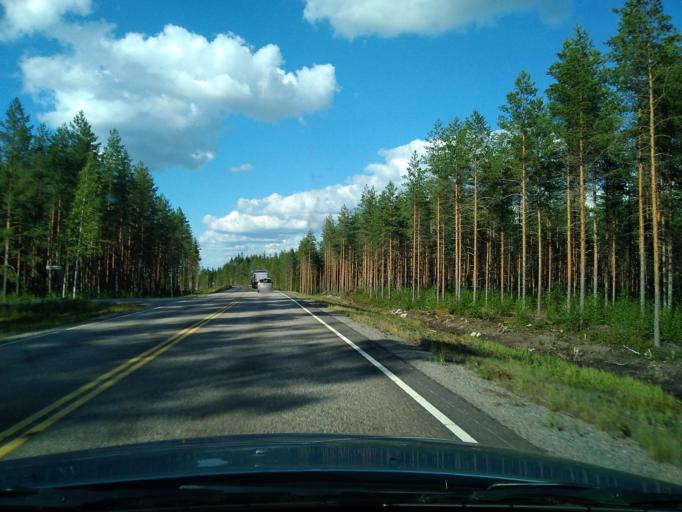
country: FI
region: Central Finland
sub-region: Keuruu
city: Keuruu
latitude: 62.1484
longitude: 24.7489
